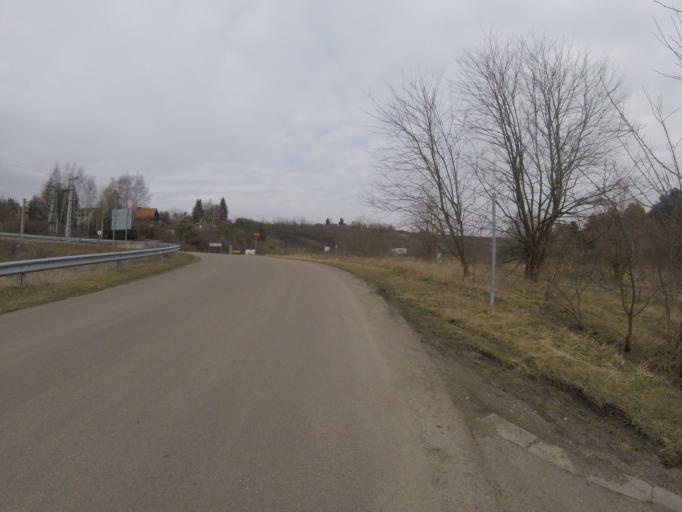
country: HU
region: Heves
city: Egerszalok
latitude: 47.8593
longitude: 20.3354
